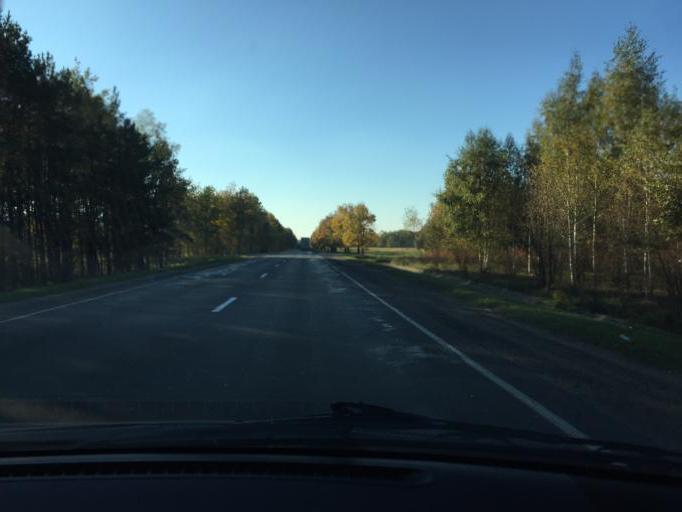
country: BY
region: Brest
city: Luninyets
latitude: 52.2744
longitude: 26.8964
